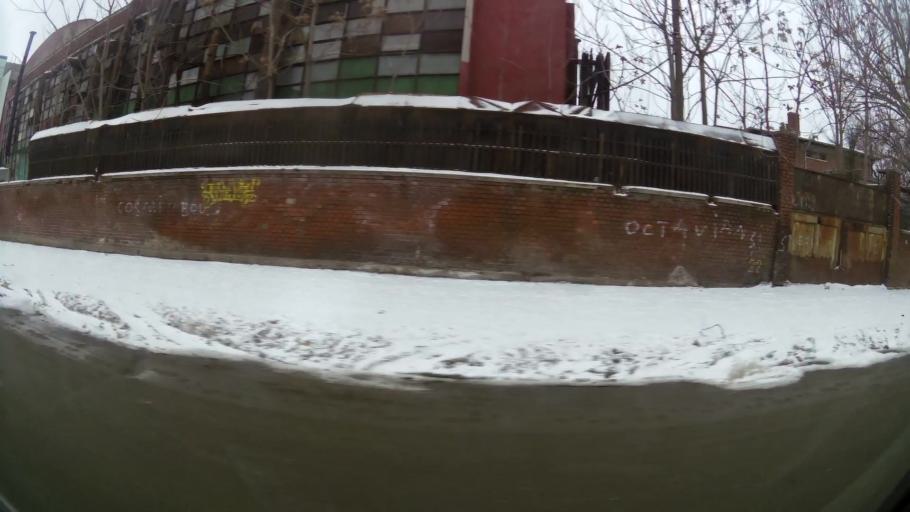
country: RO
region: Prahova
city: Ploiesti
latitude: 44.9298
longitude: 26.0403
